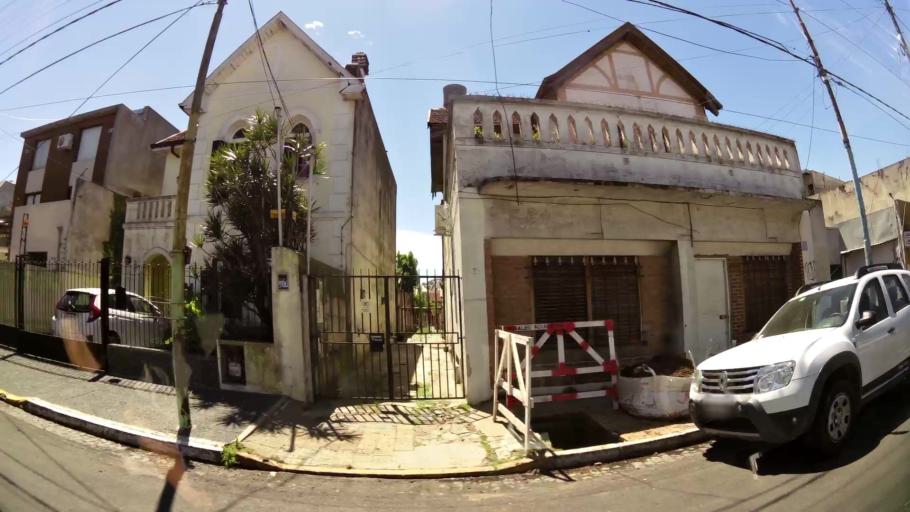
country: AR
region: Buenos Aires
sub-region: Partido de Quilmes
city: Quilmes
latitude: -34.7150
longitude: -58.2722
